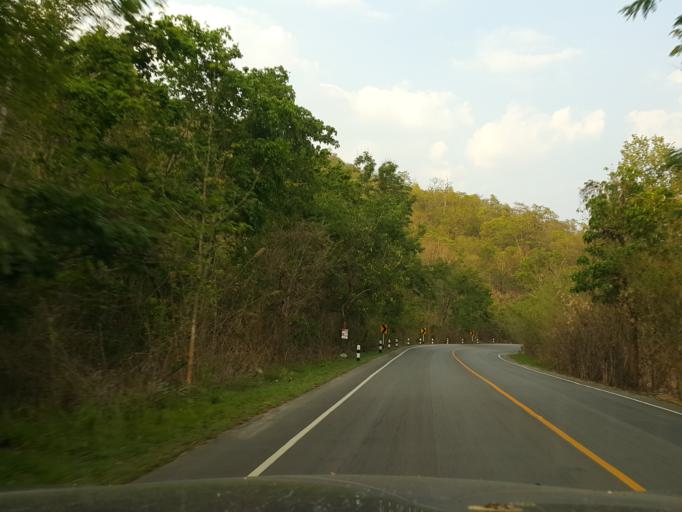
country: TH
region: Lamphun
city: Li
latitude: 17.8414
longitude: 99.0113
